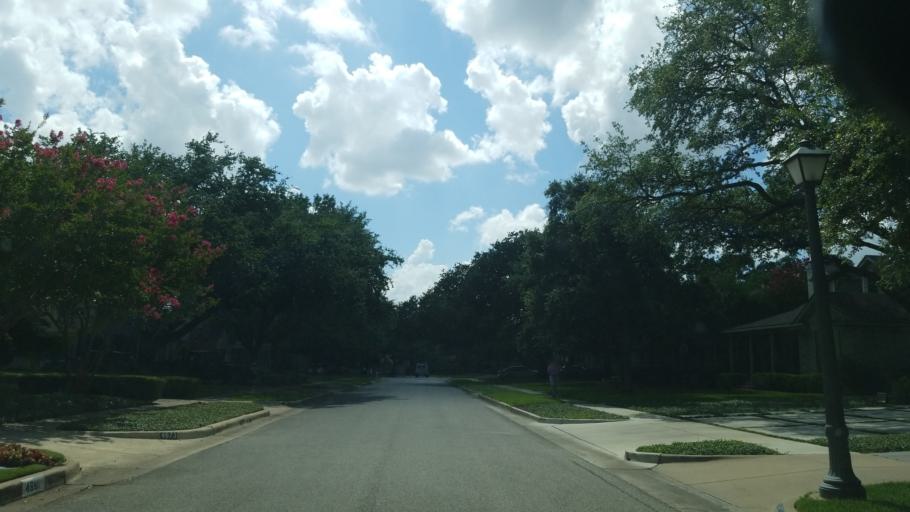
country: US
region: Texas
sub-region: Dallas County
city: University Park
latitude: 32.8314
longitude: -96.8181
